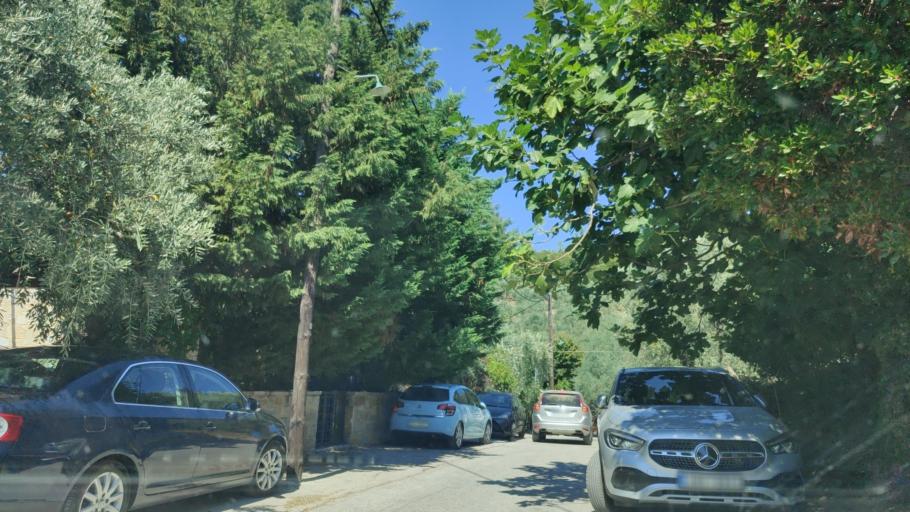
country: GR
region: East Macedonia and Thrace
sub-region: Nomos Kavalas
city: Prinos
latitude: 40.7924
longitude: 24.6327
